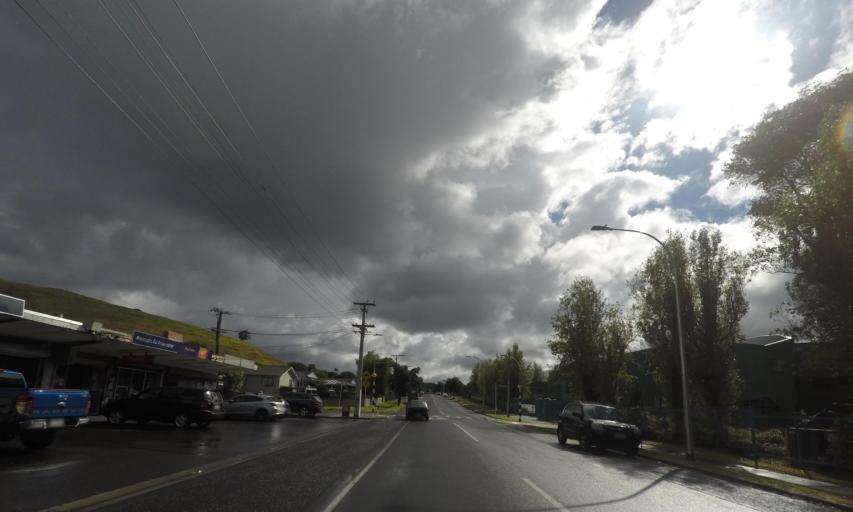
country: NZ
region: Auckland
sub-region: Auckland
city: Mangere
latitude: -36.9548
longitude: 174.7853
